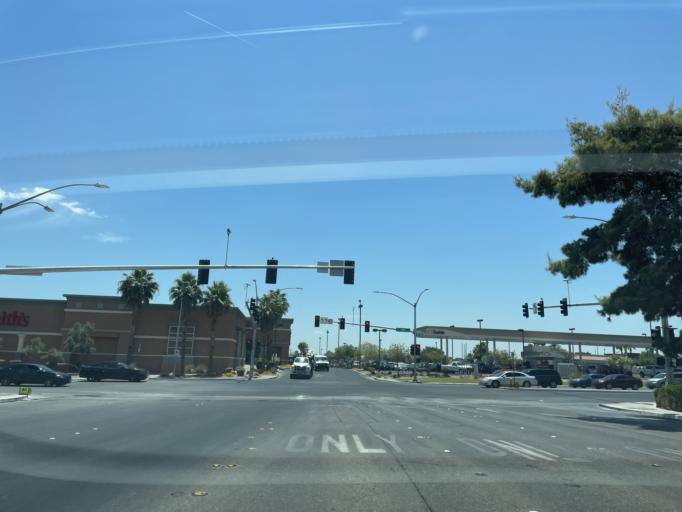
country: US
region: Nevada
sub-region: Clark County
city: North Las Vegas
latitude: 36.2622
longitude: -115.1542
